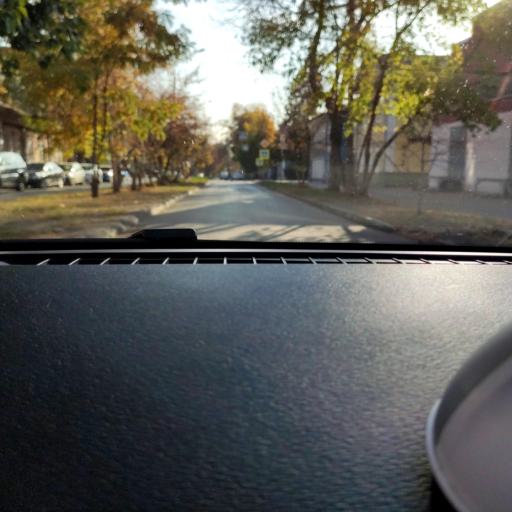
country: RU
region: Samara
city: Samara
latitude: 53.1940
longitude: 50.1111
